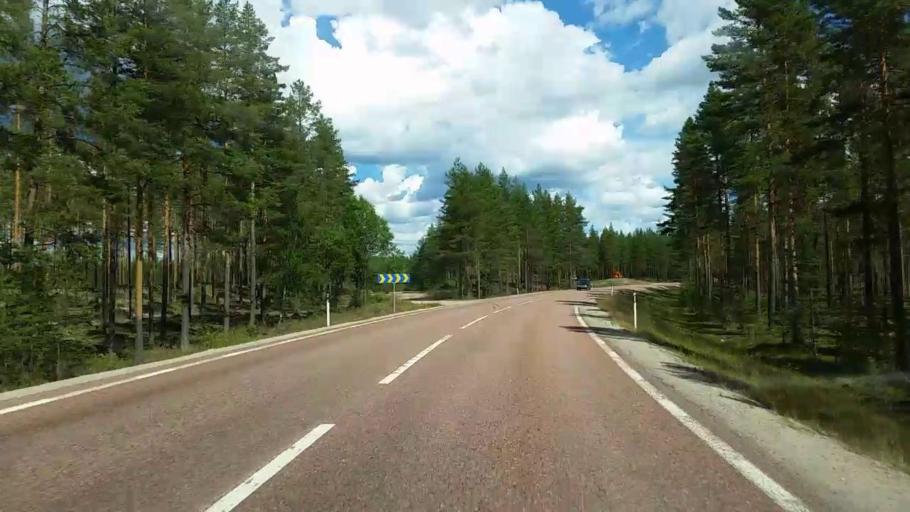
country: SE
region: Gaevleborg
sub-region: Ovanakers Kommun
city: Edsbyn
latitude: 61.3512
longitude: 15.5784
